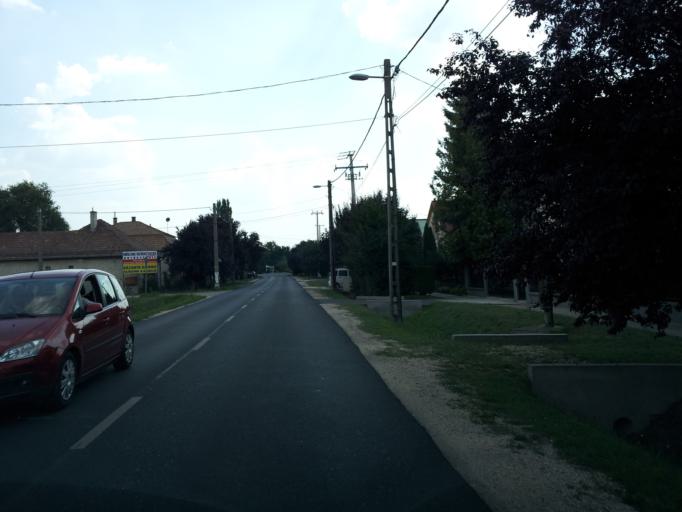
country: HU
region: Pest
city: Toekoel
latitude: 47.3351
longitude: 18.9667
